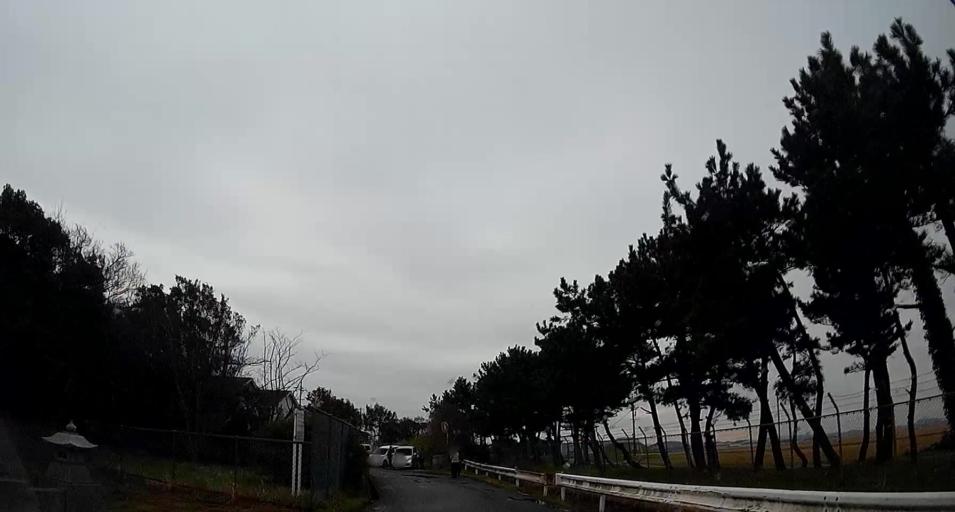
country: JP
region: Chiba
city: Kisarazu
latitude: 35.4052
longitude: 139.9142
